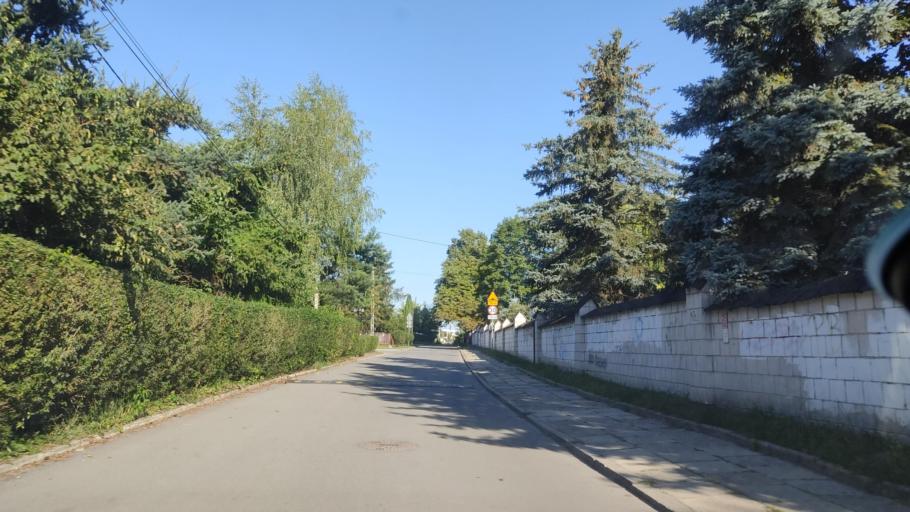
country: PL
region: Lesser Poland Voivodeship
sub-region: Powiat krakowski
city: Zielonki
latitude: 50.0967
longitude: 19.9296
